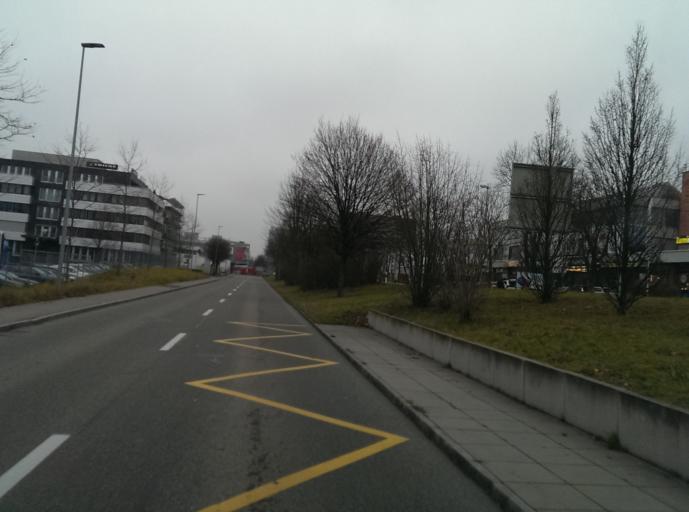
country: CH
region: Aargau
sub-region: Bezirk Baden
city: Spreitenbach
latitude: 47.4296
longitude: 8.3595
